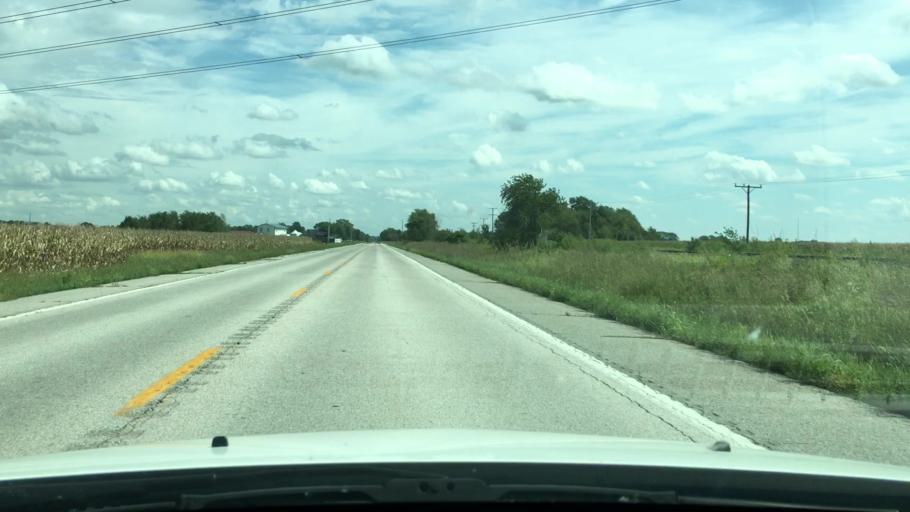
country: US
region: Missouri
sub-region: Audrain County
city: Vandalia
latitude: 39.2917
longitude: -91.5381
